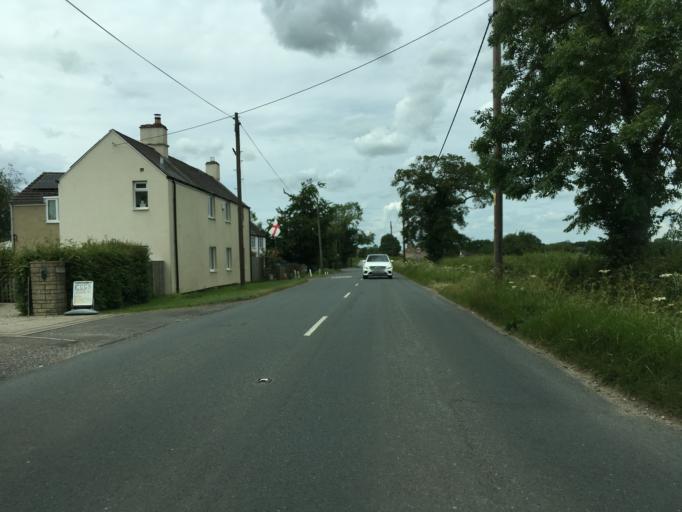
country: GB
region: England
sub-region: Wiltshire
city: Lyneham
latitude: 51.5638
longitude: -1.9537
